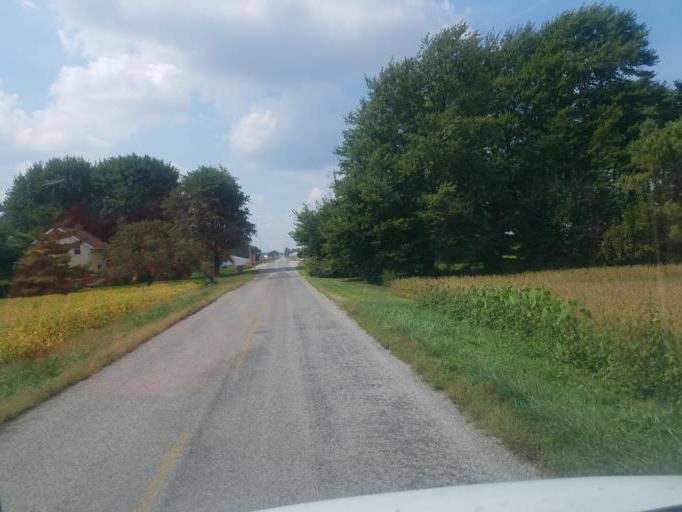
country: US
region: Ohio
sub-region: Hardin County
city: Ada
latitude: 40.6377
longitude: -83.8055
